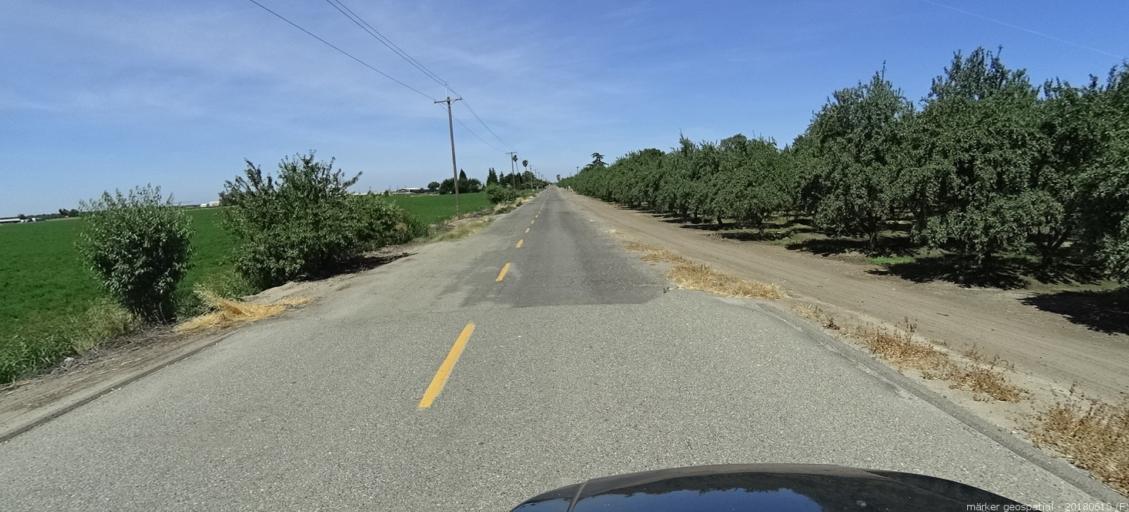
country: US
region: California
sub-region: Madera County
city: Chowchilla
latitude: 37.0400
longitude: -120.2970
